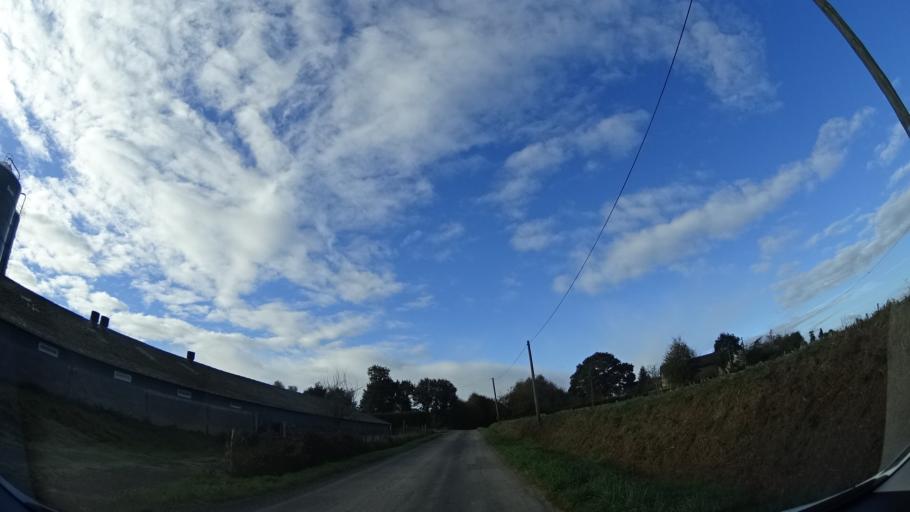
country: FR
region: Brittany
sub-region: Departement d'Ille-et-Vilaine
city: Geveze
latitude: 48.1996
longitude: -1.8113
